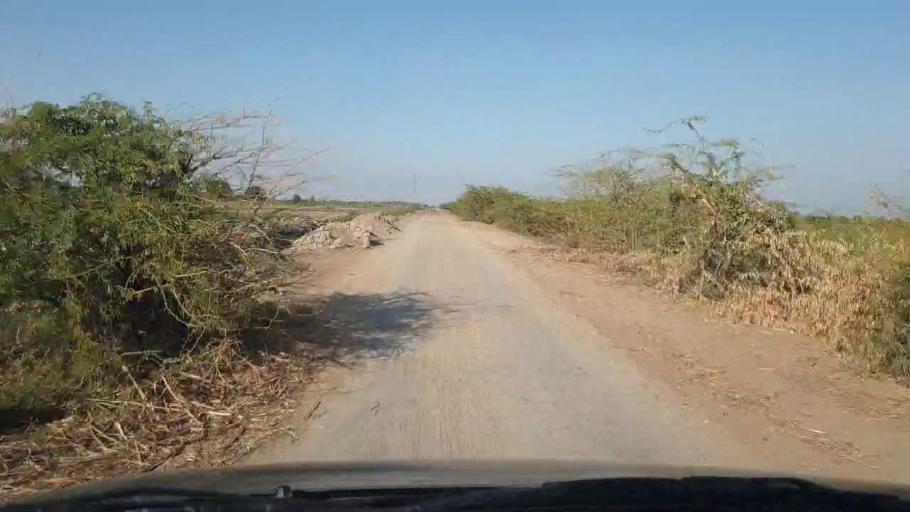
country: PK
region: Sindh
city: Samaro
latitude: 25.1460
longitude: 69.3067
